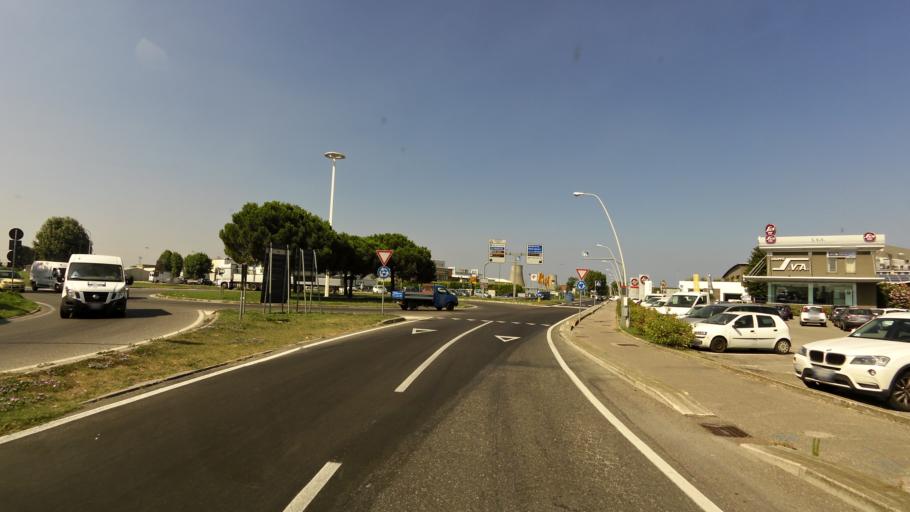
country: IT
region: Emilia-Romagna
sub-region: Provincia di Ravenna
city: Ravenna
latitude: 44.4246
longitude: 12.2278
